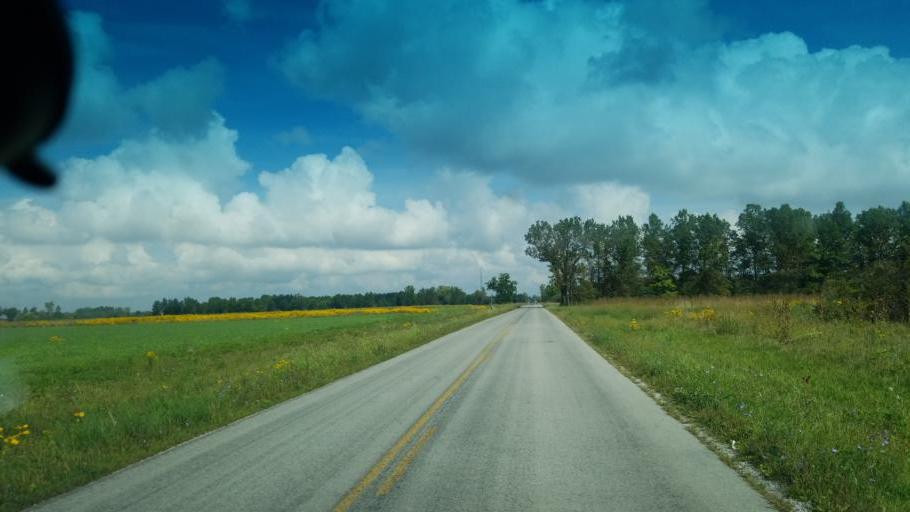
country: US
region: Ohio
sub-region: Wyandot County
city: Carey
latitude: 40.9203
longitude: -83.3818
